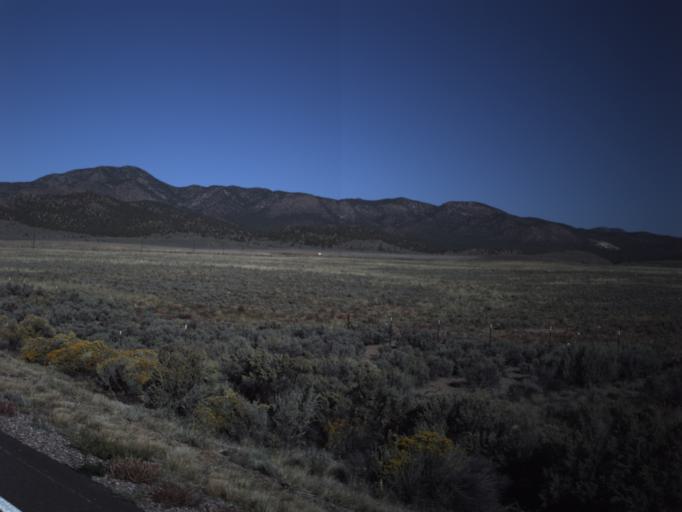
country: US
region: Utah
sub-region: Washington County
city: Enterprise
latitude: 37.8028
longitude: -113.9213
